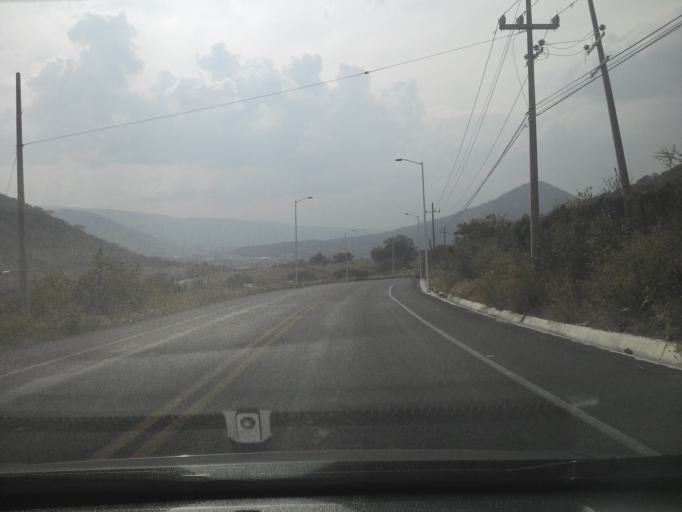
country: MX
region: Jalisco
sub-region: Tlajomulco de Zuniga
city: Lomas del Sur
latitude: 20.4837
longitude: -103.4298
